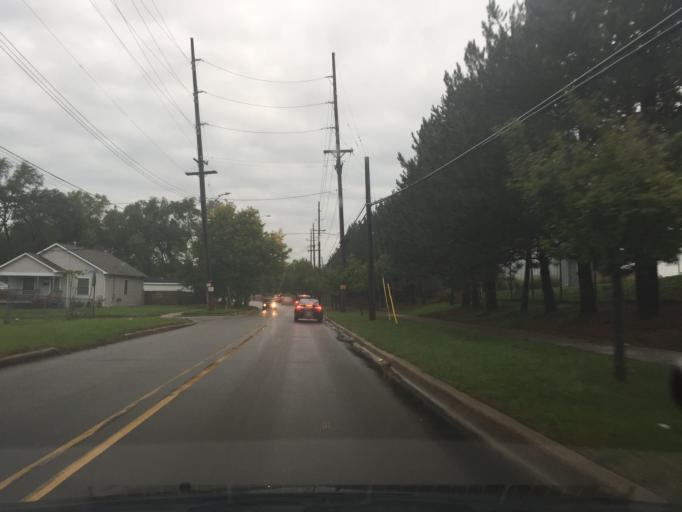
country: US
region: Michigan
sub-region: Oakland County
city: Pontiac
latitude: 42.6240
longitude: -83.2884
